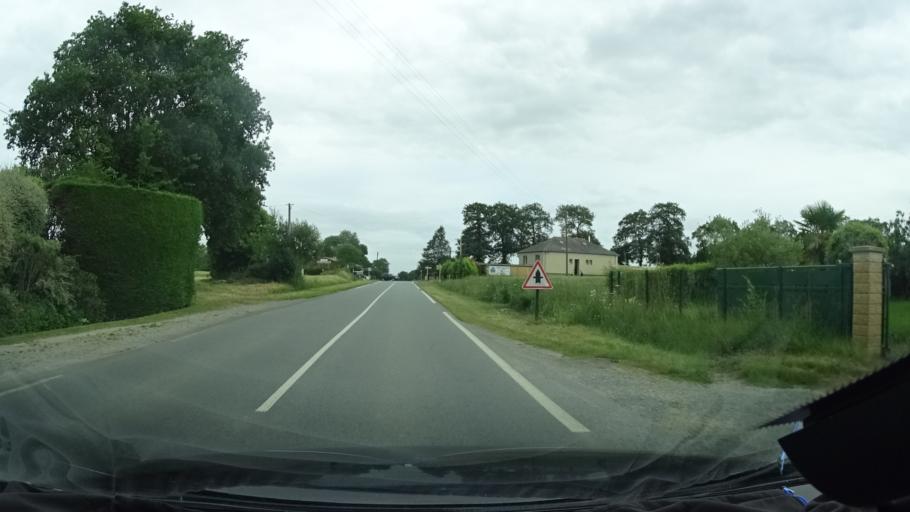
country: FR
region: Brittany
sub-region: Departement d'Ille-et-Vilaine
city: Le Minihic-sur-Rance
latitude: 48.5844
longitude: -2.0205
